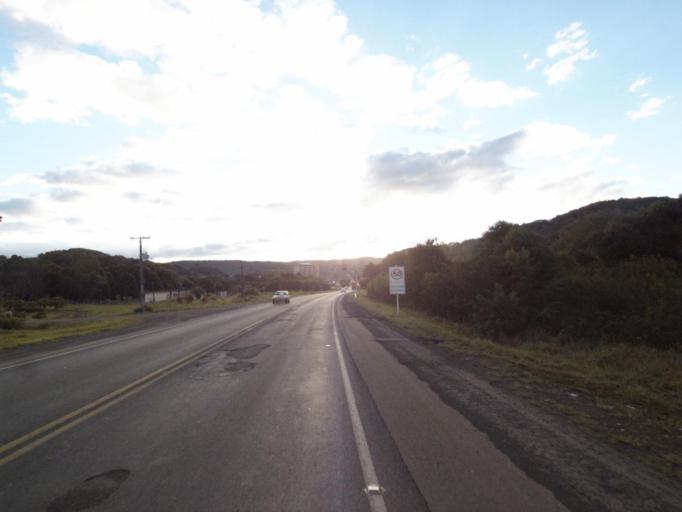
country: BR
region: Santa Catarina
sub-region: Joacaba
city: Joacaba
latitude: -27.2864
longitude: -51.4298
